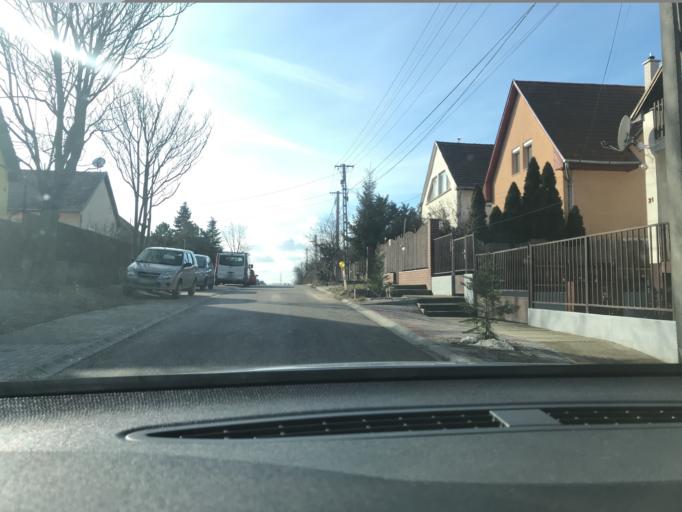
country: HU
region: Pest
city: Fot
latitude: 47.6295
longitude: 19.1756
